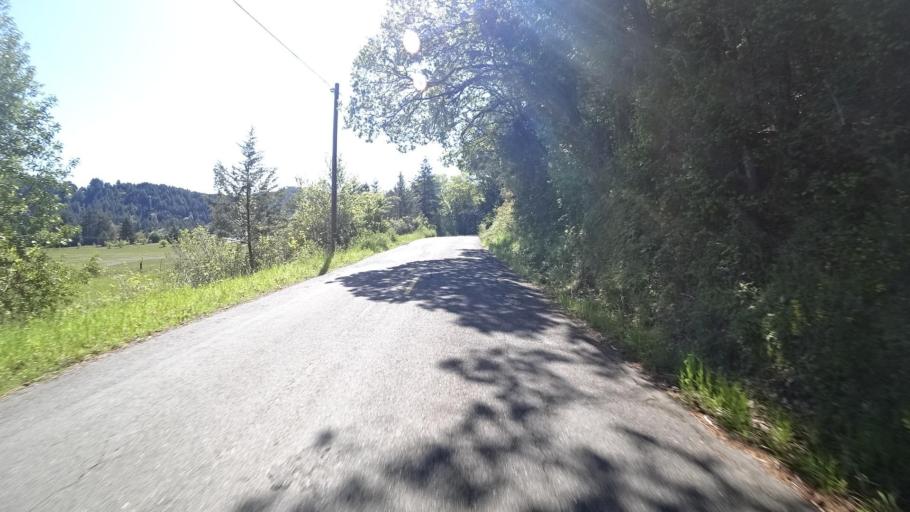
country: US
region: California
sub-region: Humboldt County
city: Rio Dell
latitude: 40.2374
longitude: -124.1602
